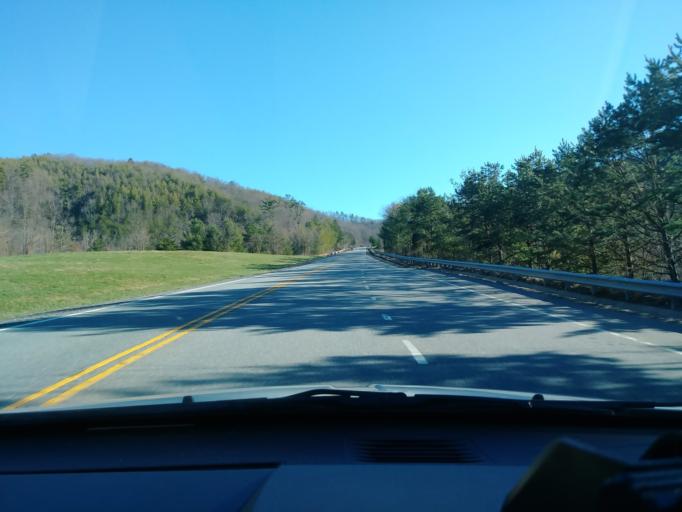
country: US
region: North Carolina
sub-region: Madison County
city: Marshall
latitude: 35.9028
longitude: -82.8014
